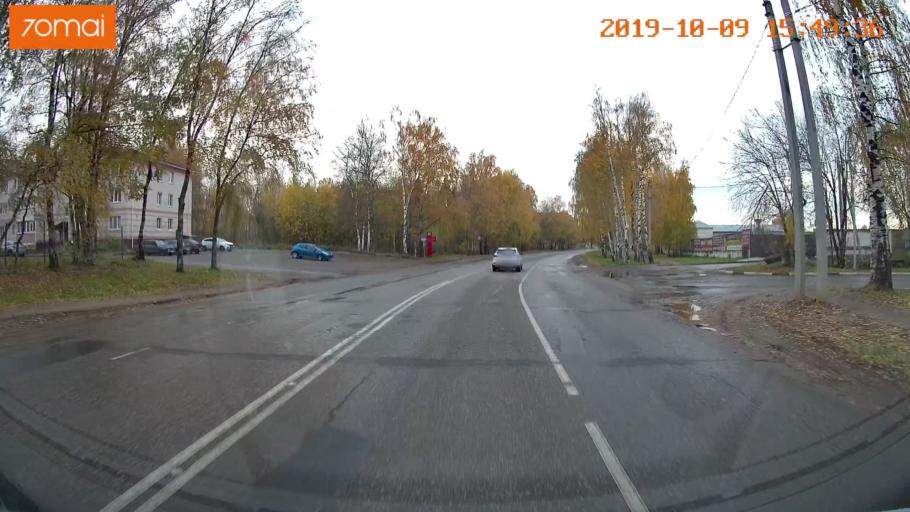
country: RU
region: Kostroma
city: Oktyabr'skiy
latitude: 57.8041
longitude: 41.0027
